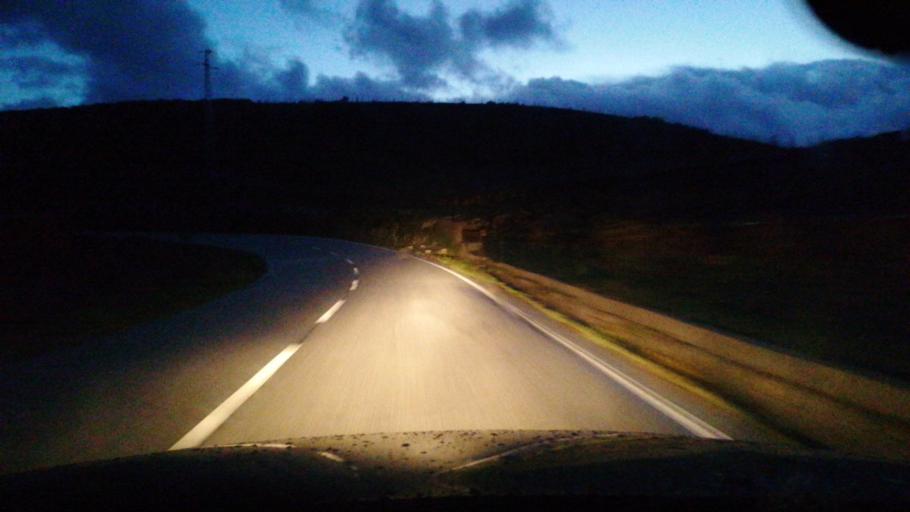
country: PT
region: Viseu
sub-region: Tabuaco
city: Tabuaco
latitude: 41.1319
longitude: -7.5202
